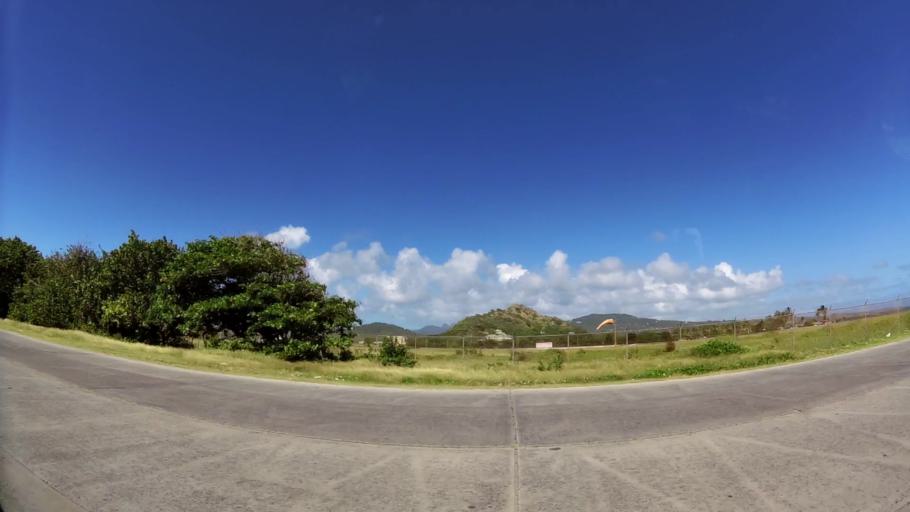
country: LC
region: Vieux-Fort
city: Vieux Fort
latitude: 13.7318
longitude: -60.9415
